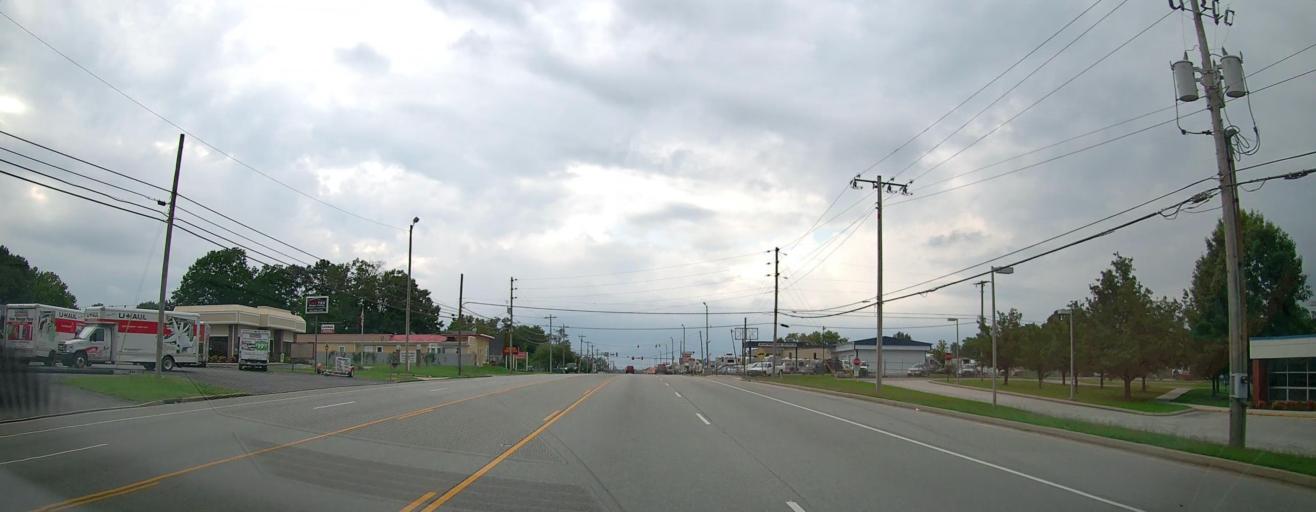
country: US
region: Tennessee
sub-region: Coffee County
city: Manchester
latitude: 35.4672
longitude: -86.0706
